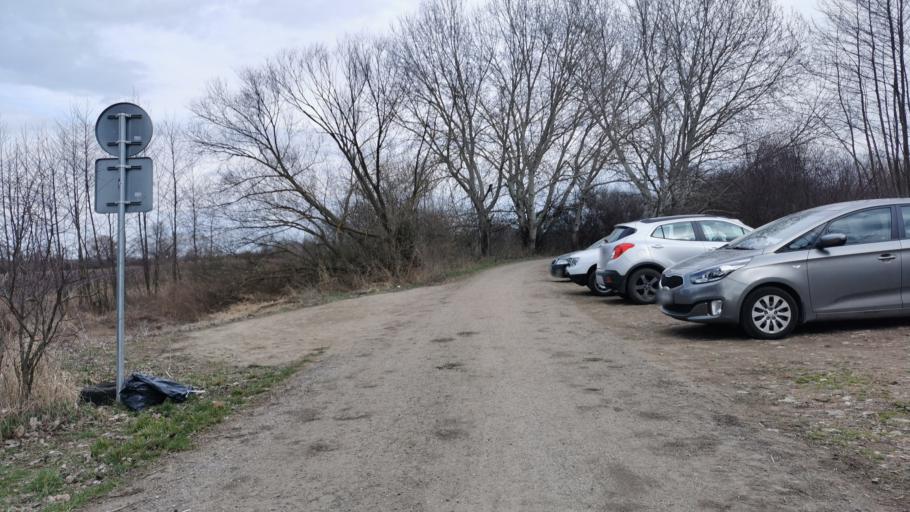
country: SK
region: Trnavsky
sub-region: Okres Skalica
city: Holic
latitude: 48.8001
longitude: 17.1172
